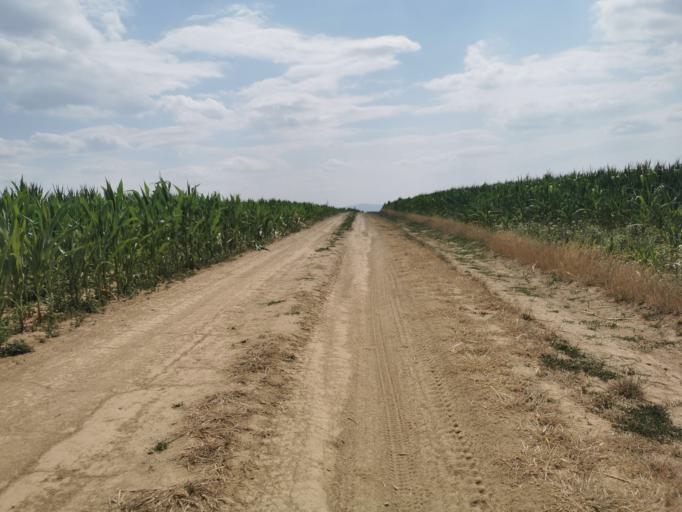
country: SK
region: Trnavsky
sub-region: Okres Senica
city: Senica
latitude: 48.6915
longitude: 17.4209
